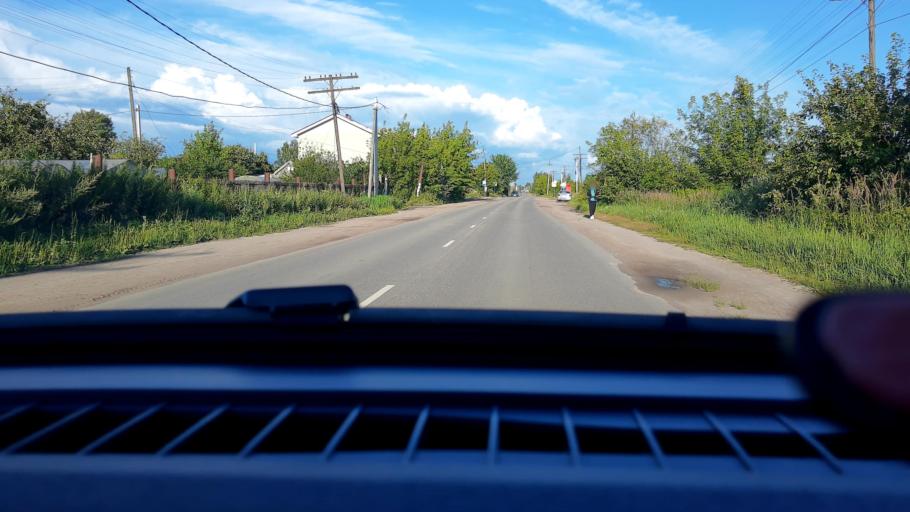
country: RU
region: Nizjnij Novgorod
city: Bor
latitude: 56.3542
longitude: 44.1024
